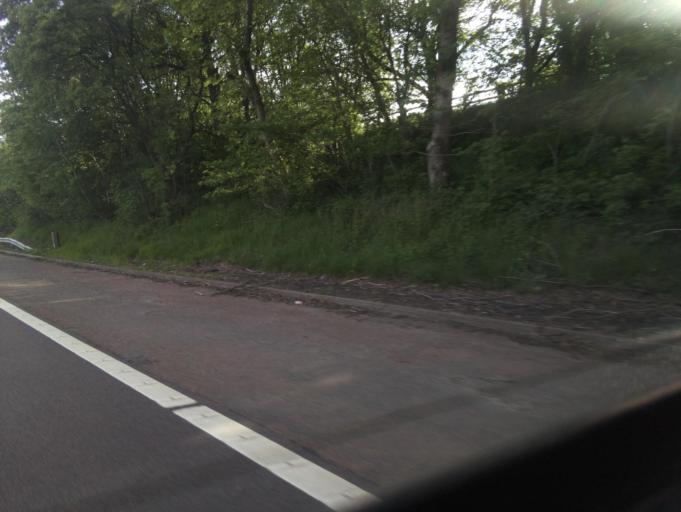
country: GB
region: Scotland
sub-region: Fife
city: Kelty
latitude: 56.1438
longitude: -3.3944
